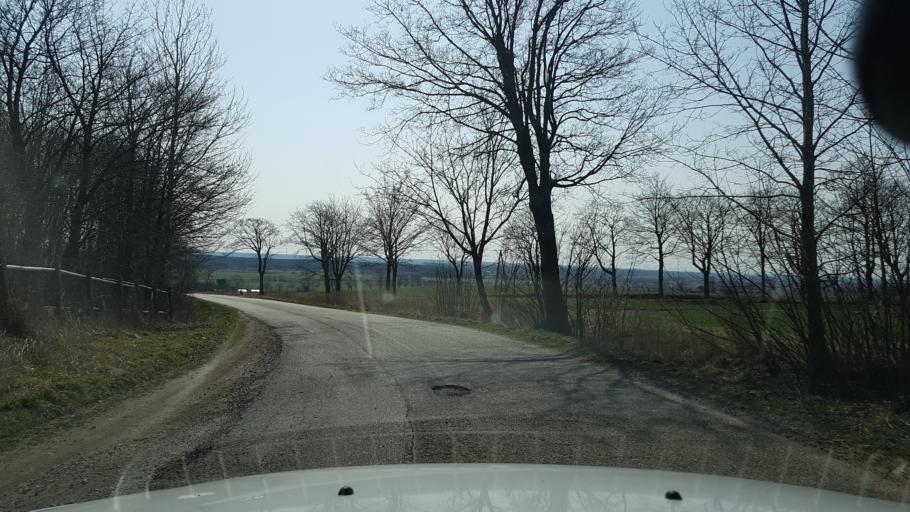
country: PL
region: West Pomeranian Voivodeship
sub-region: Powiat slawienski
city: Darlowo
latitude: 54.4655
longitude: 16.5040
